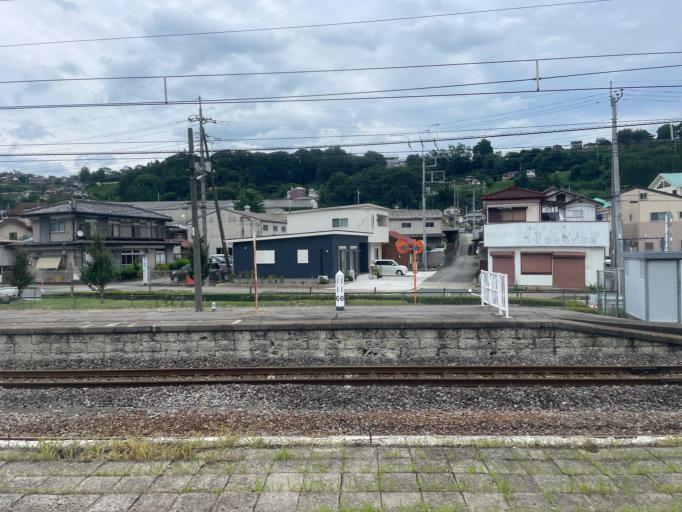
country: JP
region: Gunma
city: Numata
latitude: 36.6412
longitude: 139.0364
